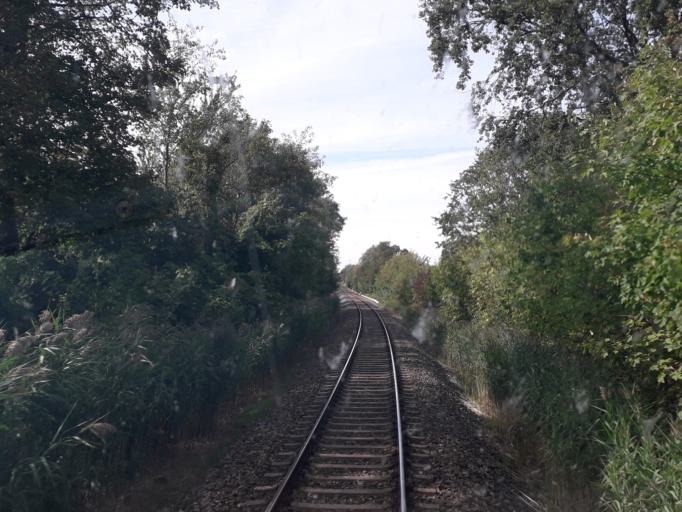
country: DE
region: Brandenburg
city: Kremmen
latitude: 52.7366
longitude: 13.0878
